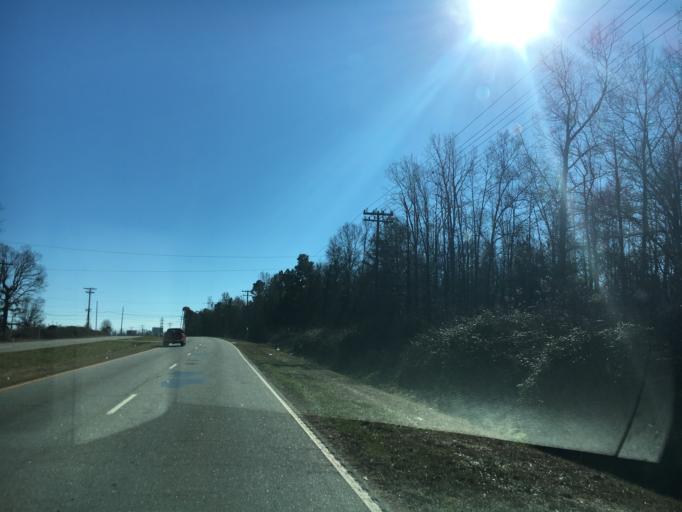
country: US
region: South Carolina
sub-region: Anderson County
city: Homeland Park
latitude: 34.4450
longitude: -82.6678
